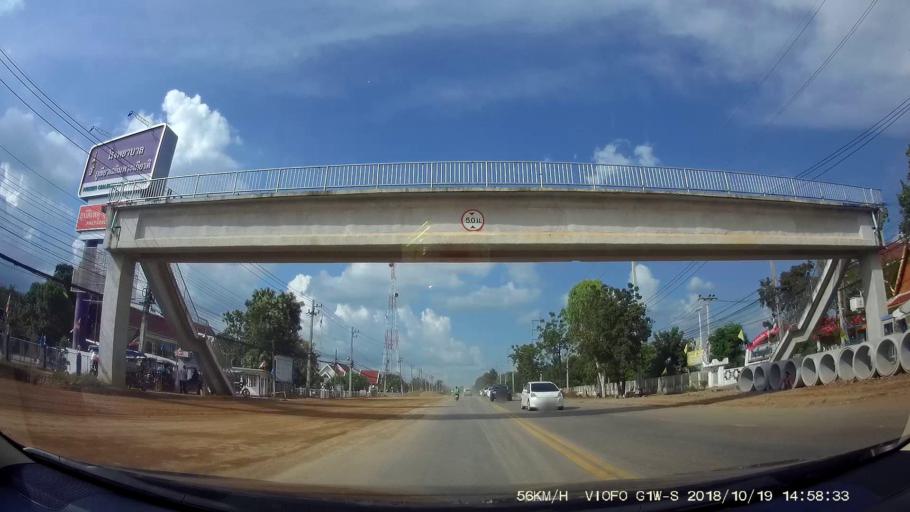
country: TH
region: Chaiyaphum
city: Phu Khiao
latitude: 16.3759
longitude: 102.1293
